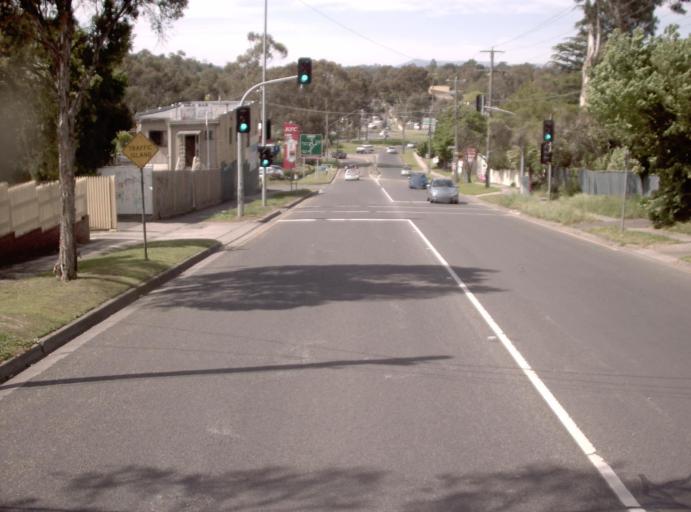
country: AU
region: Victoria
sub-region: Maroondah
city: Croydon North
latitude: -37.7907
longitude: 145.3073
